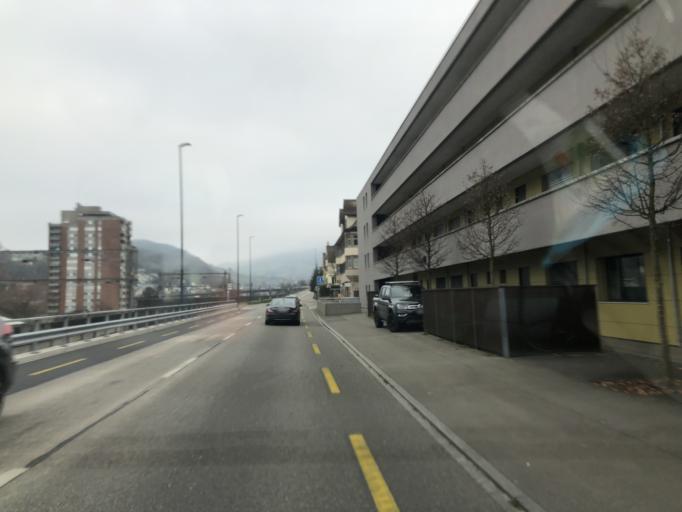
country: CH
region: Aargau
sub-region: Bezirk Baden
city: Obersiggenthal
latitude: 47.4834
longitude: 8.2922
